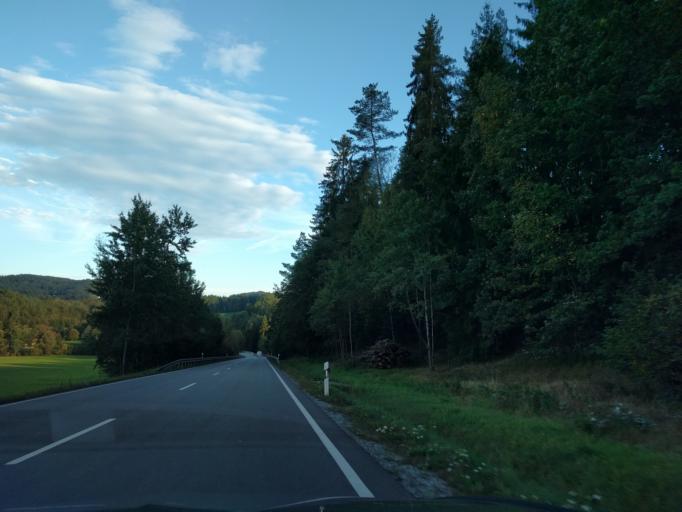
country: DE
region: Bavaria
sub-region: Lower Bavaria
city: Viechtach
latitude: 49.0589
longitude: 12.9089
